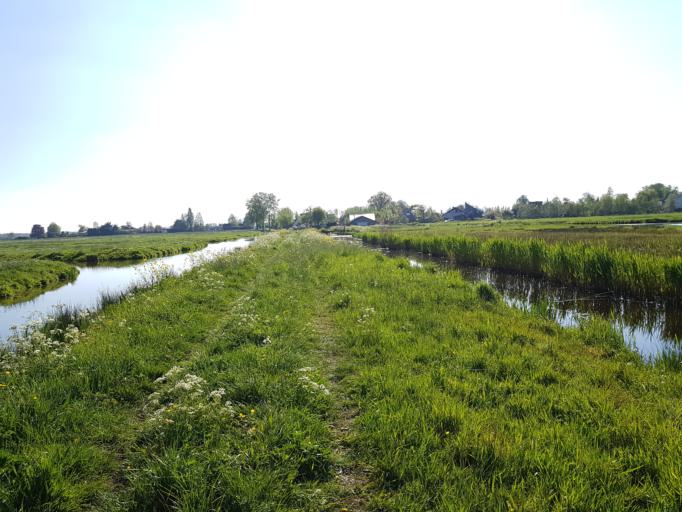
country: NL
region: South Holland
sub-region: Molenwaard
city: Nieuw-Lekkerland
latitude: 51.9453
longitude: 4.7234
